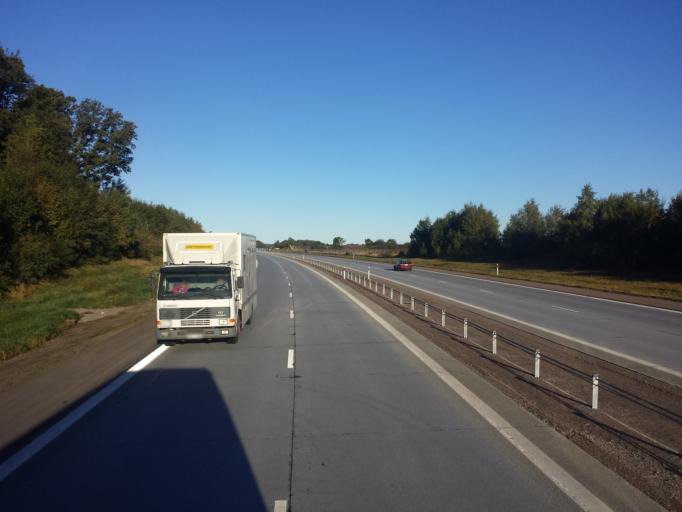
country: SE
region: Halland
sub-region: Halmstads Kommun
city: Getinge
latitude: 56.8653
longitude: 12.6567
